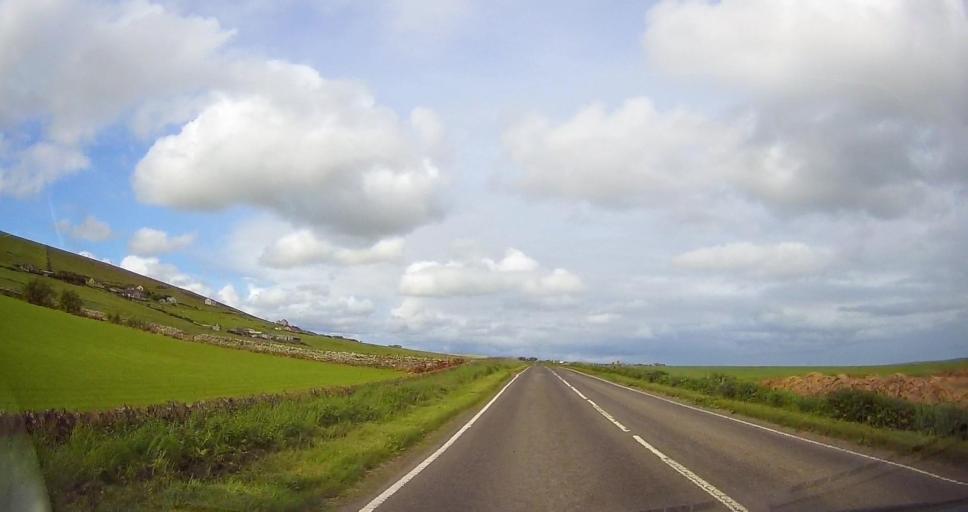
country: GB
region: Scotland
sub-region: Orkney Islands
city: Orkney
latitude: 59.0135
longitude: -3.1091
